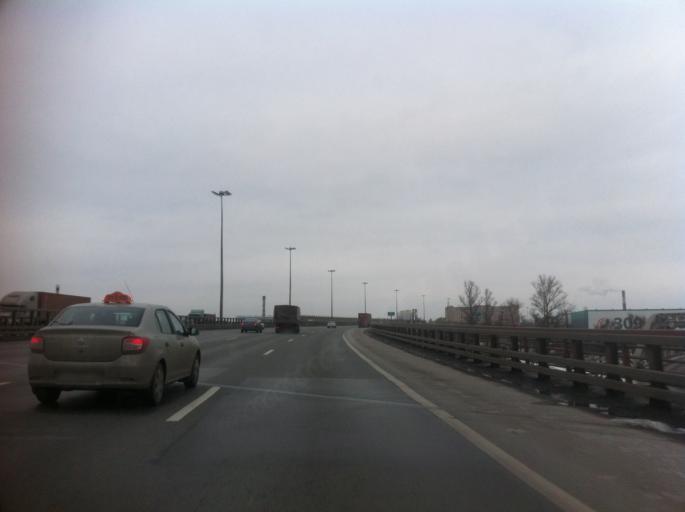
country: RU
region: St.-Petersburg
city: Obukhovo
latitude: 59.8439
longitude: 30.4573
